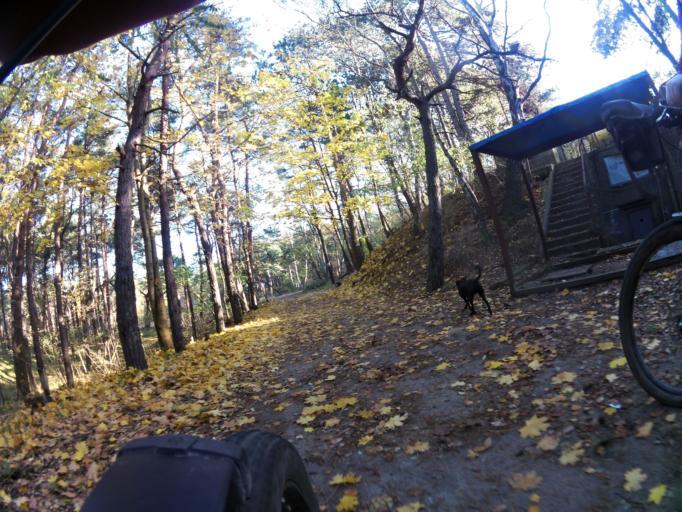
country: PL
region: Pomeranian Voivodeship
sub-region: Powiat pucki
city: Hel
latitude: 54.5960
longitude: 18.8109
